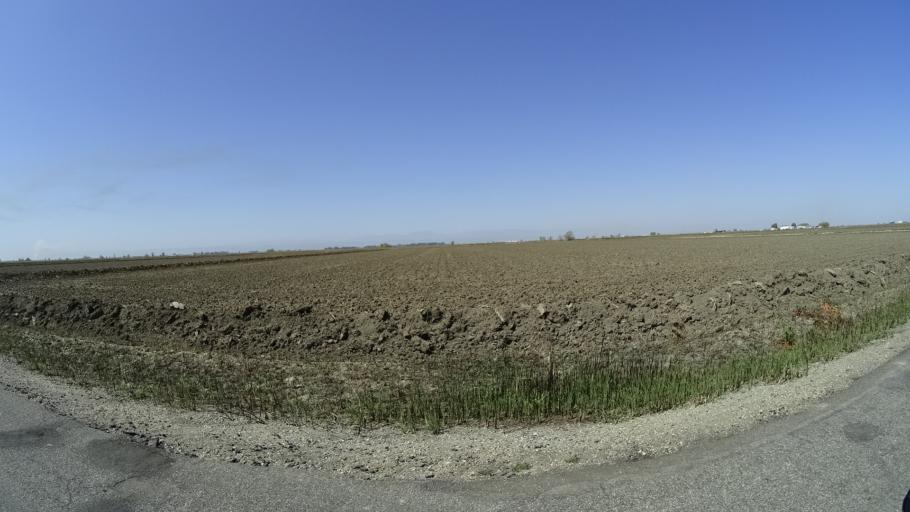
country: US
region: California
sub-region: Glenn County
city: Willows
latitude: 39.4493
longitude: -122.0643
